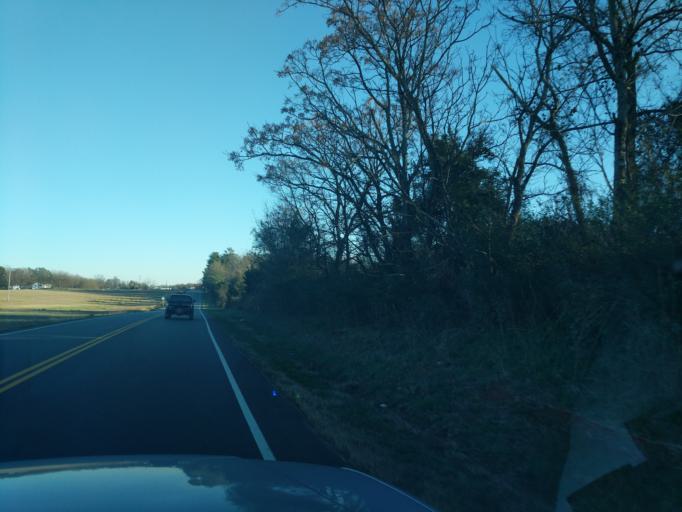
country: US
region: South Carolina
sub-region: Oconee County
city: Utica
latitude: 34.5849
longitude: -82.9254
